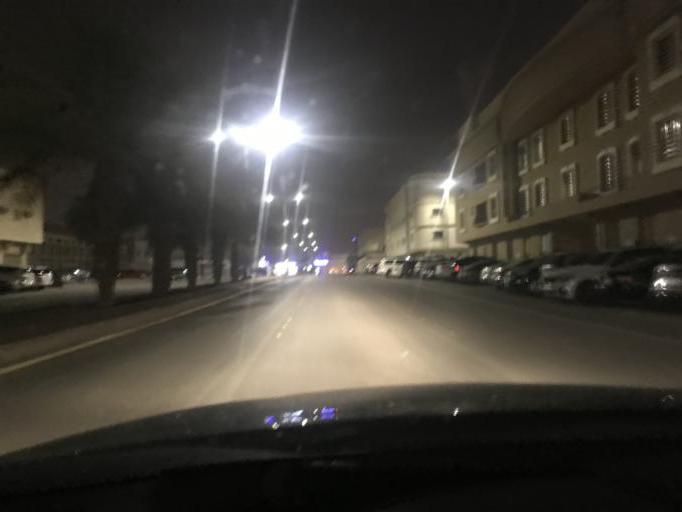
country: SA
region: Ar Riyad
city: Riyadh
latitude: 24.7332
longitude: 46.7812
